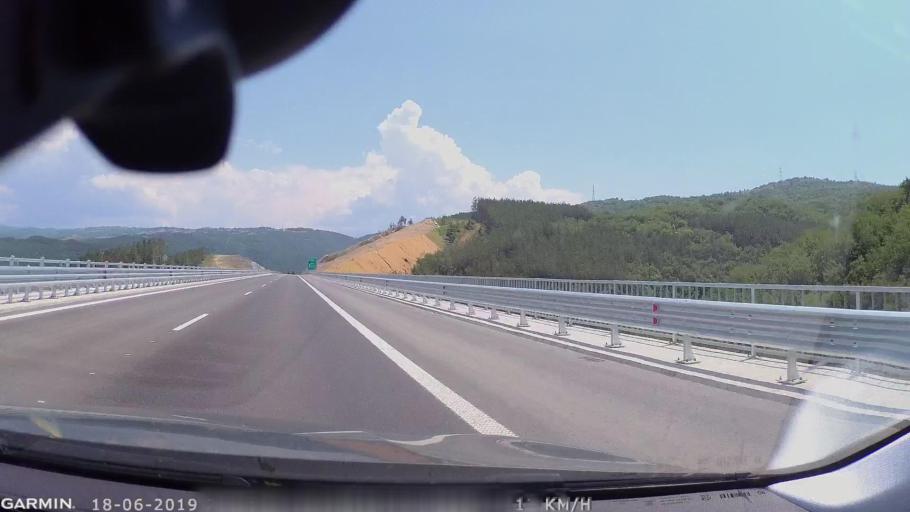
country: BG
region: Blagoevgrad
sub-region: Obshtina Blagoevgrad
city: Blagoevgrad
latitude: 41.9718
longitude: 23.0815
